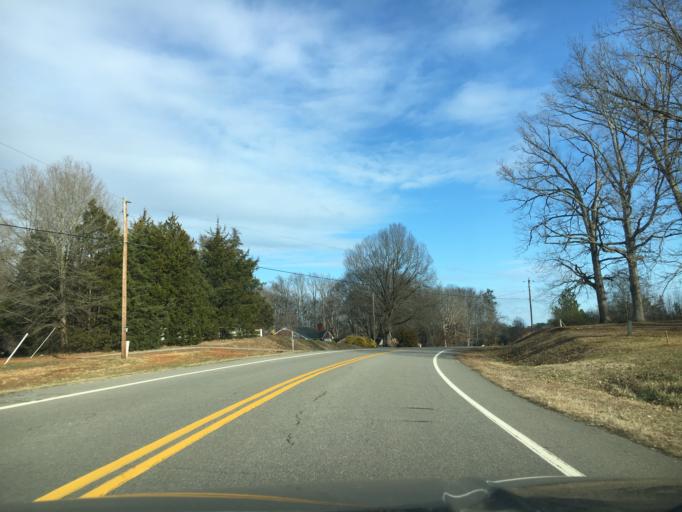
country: US
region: Virginia
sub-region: Halifax County
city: South Boston
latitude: 36.7355
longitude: -78.8503
